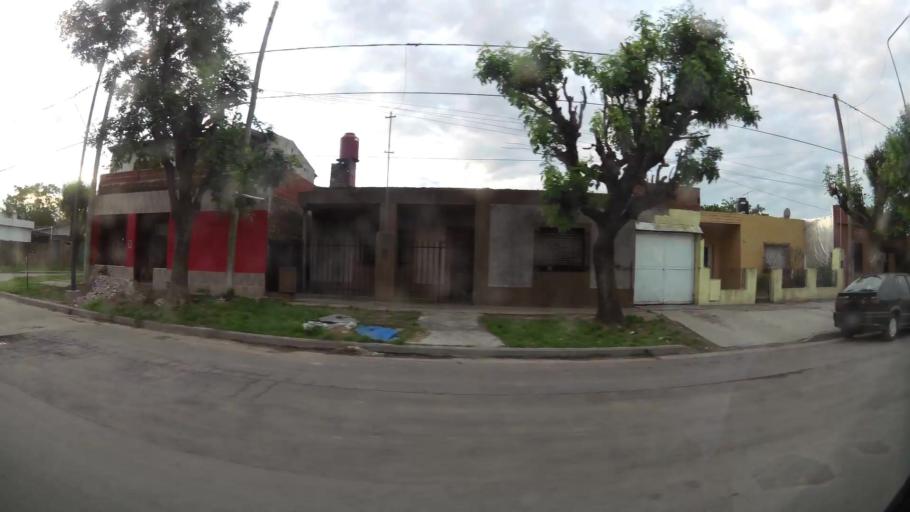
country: AR
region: Buenos Aires
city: San Nicolas de los Arroyos
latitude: -33.3179
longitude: -60.2403
